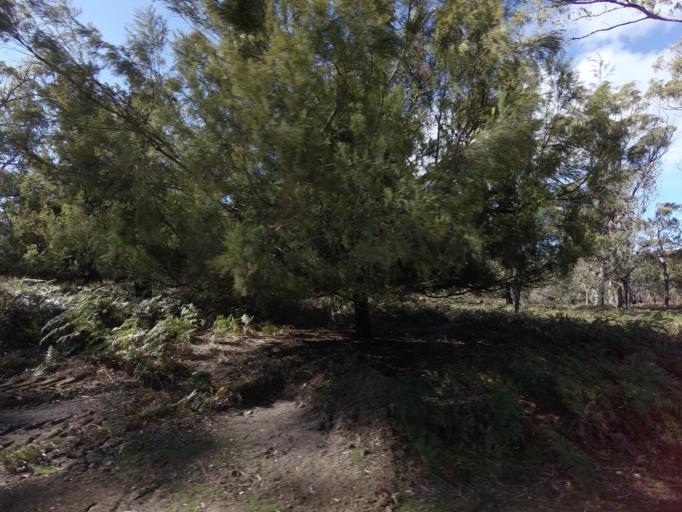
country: AU
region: Tasmania
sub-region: Clarence
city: Sandford
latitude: -42.9580
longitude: 147.7044
